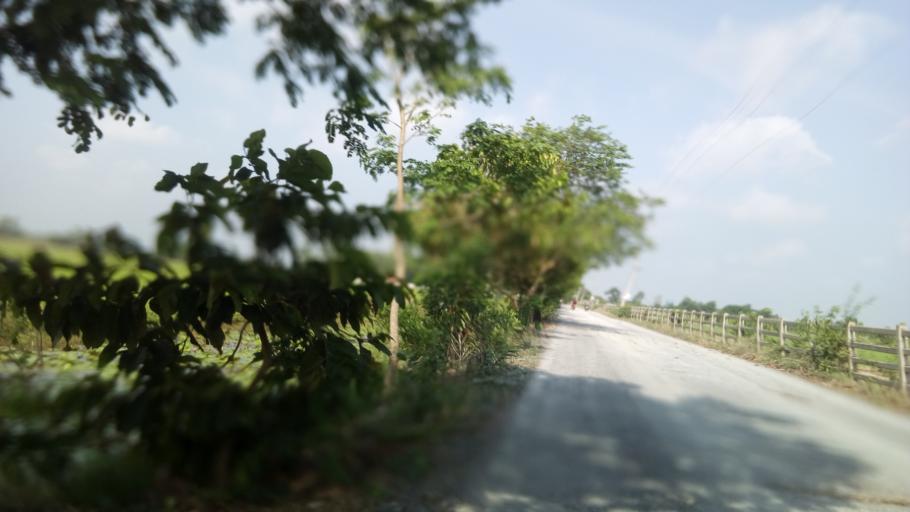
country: TH
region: Pathum Thani
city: Nong Suea
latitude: 14.1885
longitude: 100.8396
